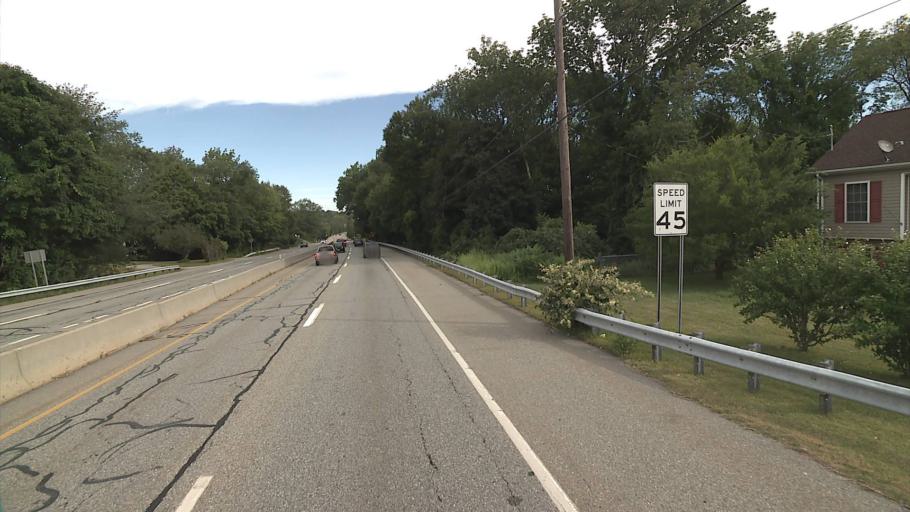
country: US
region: Connecticut
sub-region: New London County
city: Conning Towers-Nautilus Park
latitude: 41.3943
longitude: -72.1054
